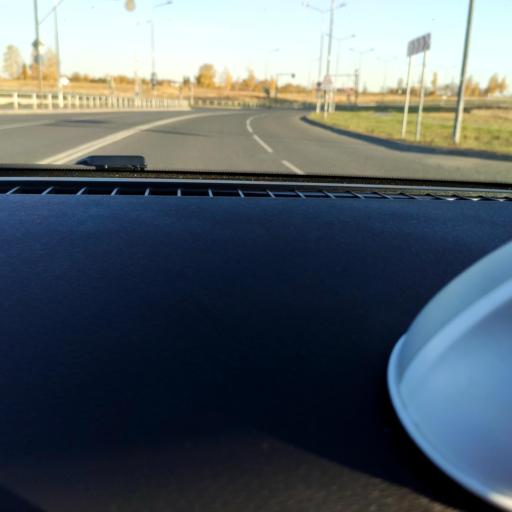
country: RU
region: Samara
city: Samara
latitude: 53.2905
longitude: 50.2328
